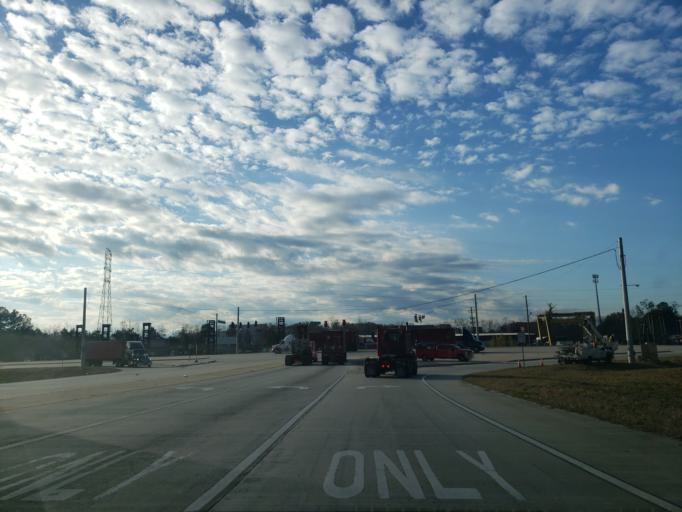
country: US
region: Georgia
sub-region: Chatham County
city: Garden City
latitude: 32.1267
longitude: -81.1642
